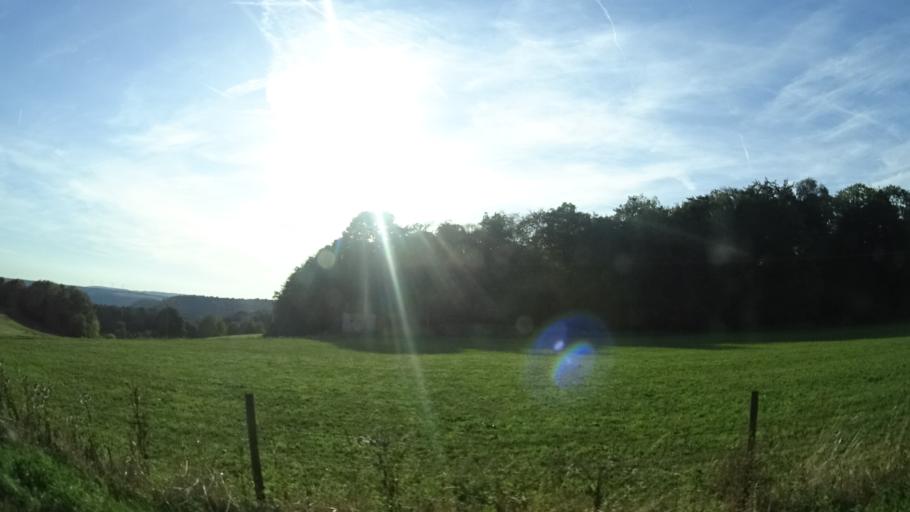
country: DE
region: Hesse
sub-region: Regierungsbezirk Darmstadt
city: Steinau an der Strasse
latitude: 50.3402
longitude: 9.3990
